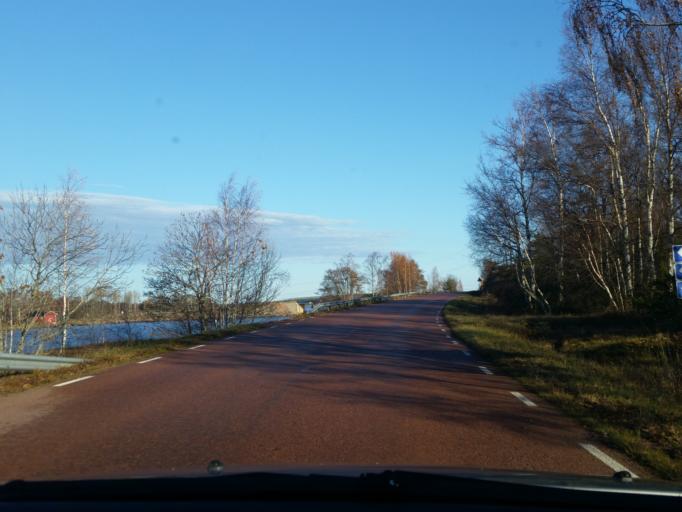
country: AX
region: Alands skaergard
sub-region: Braendoe
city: Braendoe
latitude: 60.4274
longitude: 21.0486
